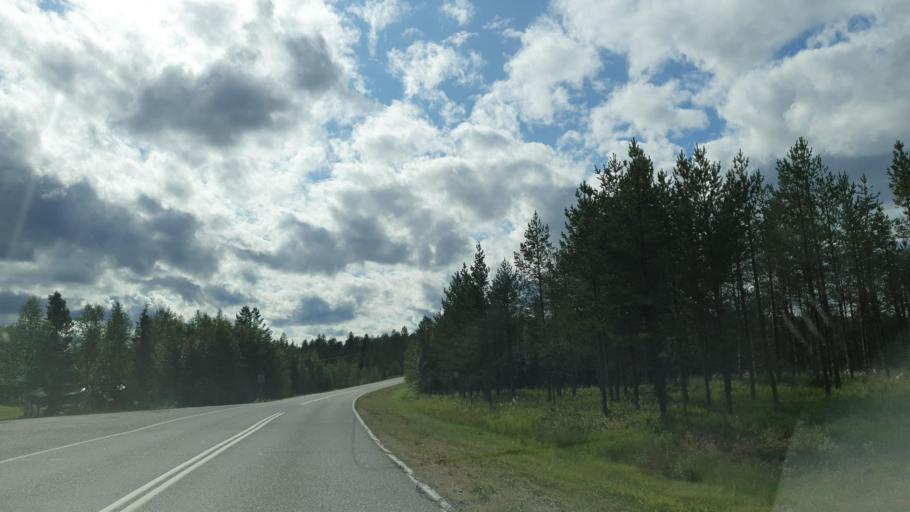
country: FI
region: Lapland
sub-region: Tunturi-Lappi
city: Muonio
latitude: 67.8769
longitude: 24.2057
